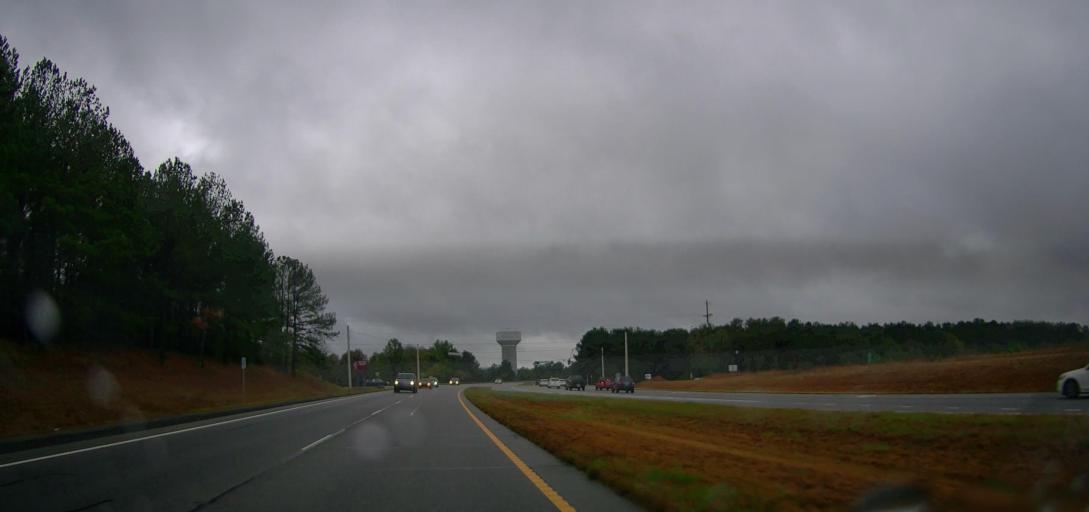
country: US
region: Georgia
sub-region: Oconee County
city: Watkinsville
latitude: 33.8510
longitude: -83.4227
